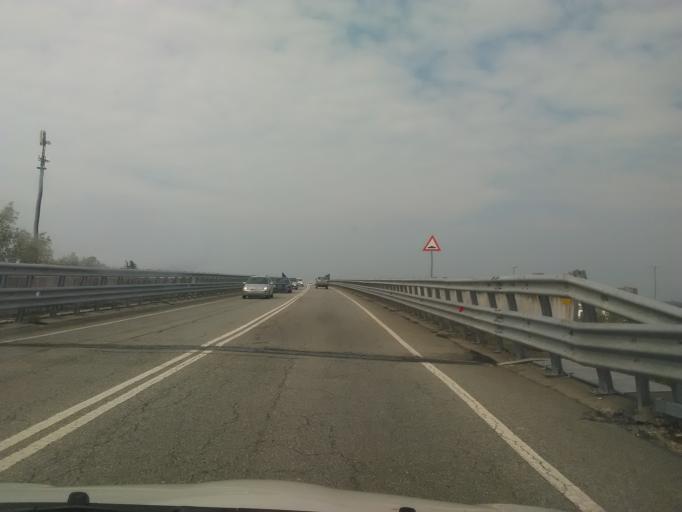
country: IT
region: Piedmont
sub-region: Provincia di Vercelli
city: Borgo d'Ale
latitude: 45.3213
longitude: 8.0753
